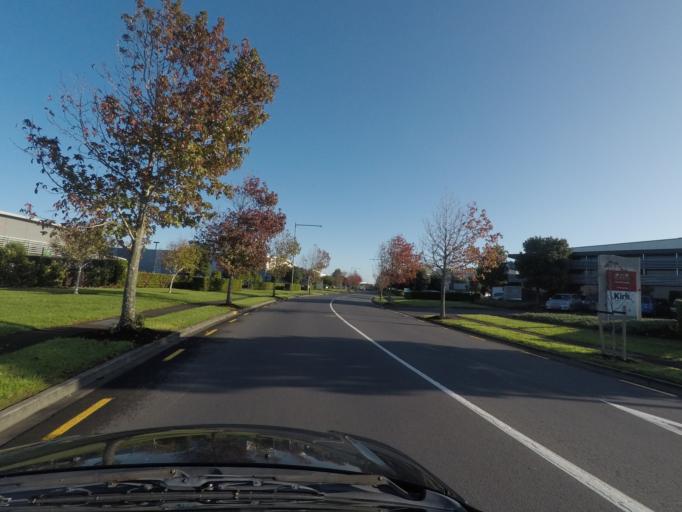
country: NZ
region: Auckland
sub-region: Auckland
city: Manukau City
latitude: -36.9406
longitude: 174.8783
